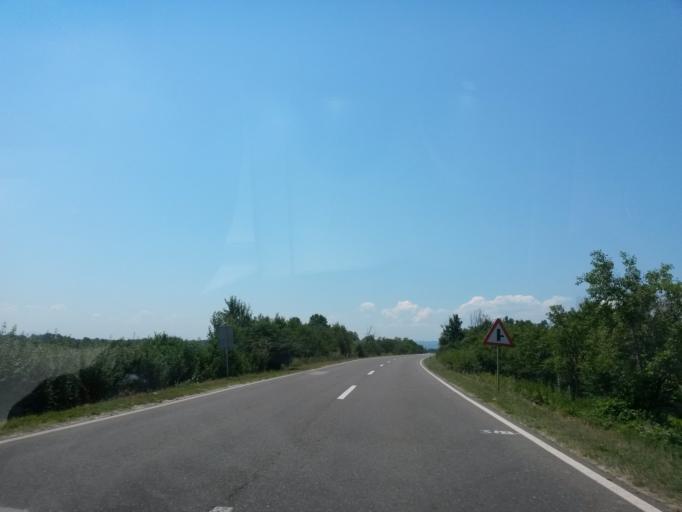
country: BA
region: Federation of Bosnia and Herzegovina
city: Donja Dubica
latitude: 45.0122
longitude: 18.3984
